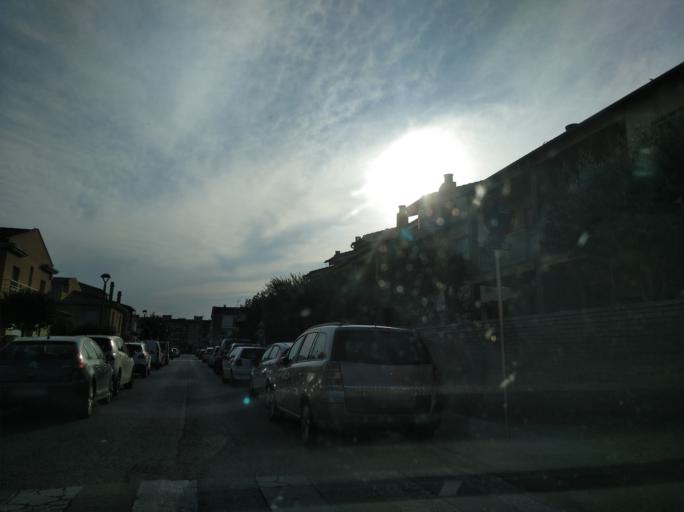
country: ES
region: Catalonia
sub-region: Provincia de Girona
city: Salt
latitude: 41.9696
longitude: 2.7910
